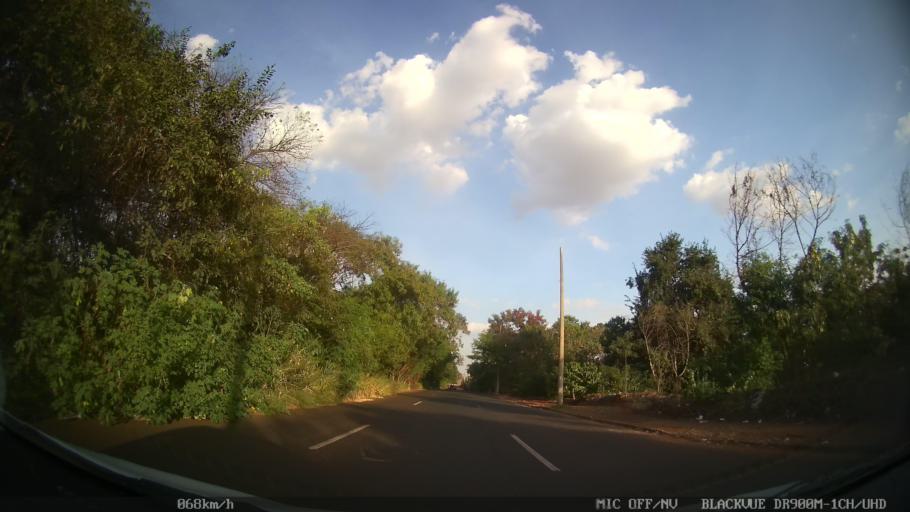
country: BR
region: Sao Paulo
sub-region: Ribeirao Preto
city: Ribeirao Preto
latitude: -21.1105
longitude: -47.8095
